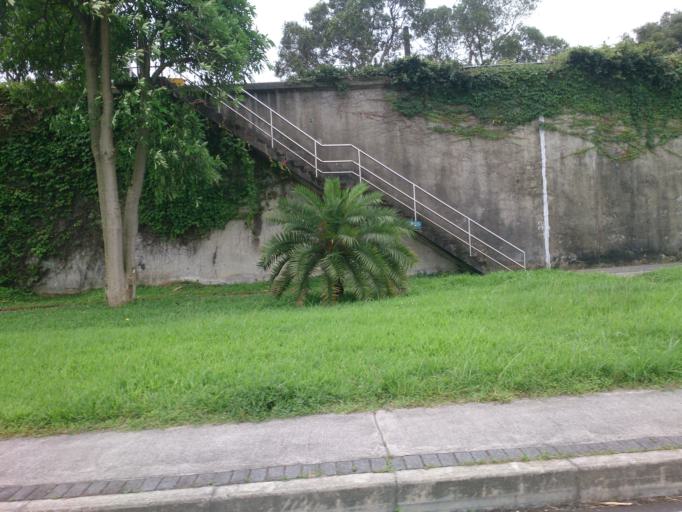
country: TW
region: Taipei
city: Taipei
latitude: 25.0536
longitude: 121.5846
